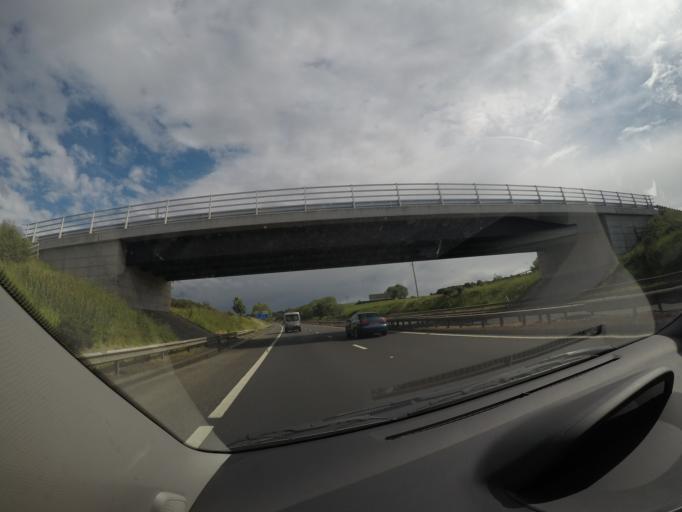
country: GB
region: Scotland
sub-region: Stirling
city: Stirling
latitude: 56.0889
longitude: -3.9456
